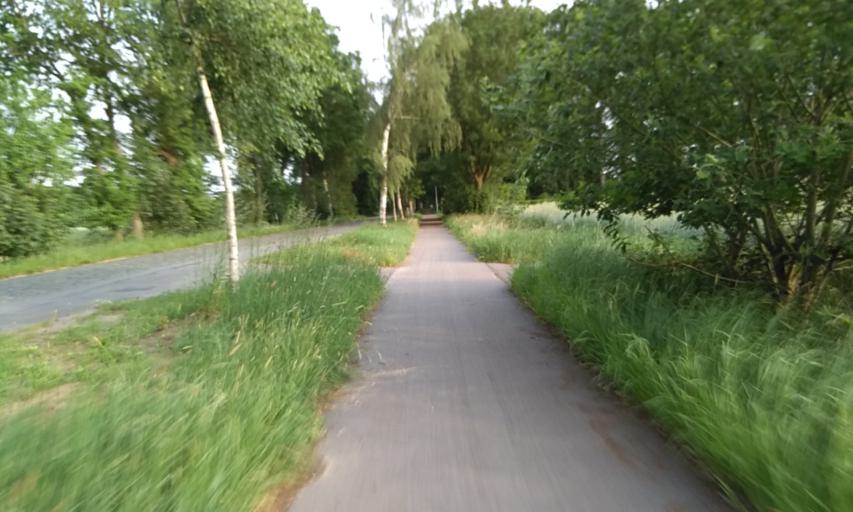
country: DE
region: Lower Saxony
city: Deinste
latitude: 53.5178
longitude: 9.4459
